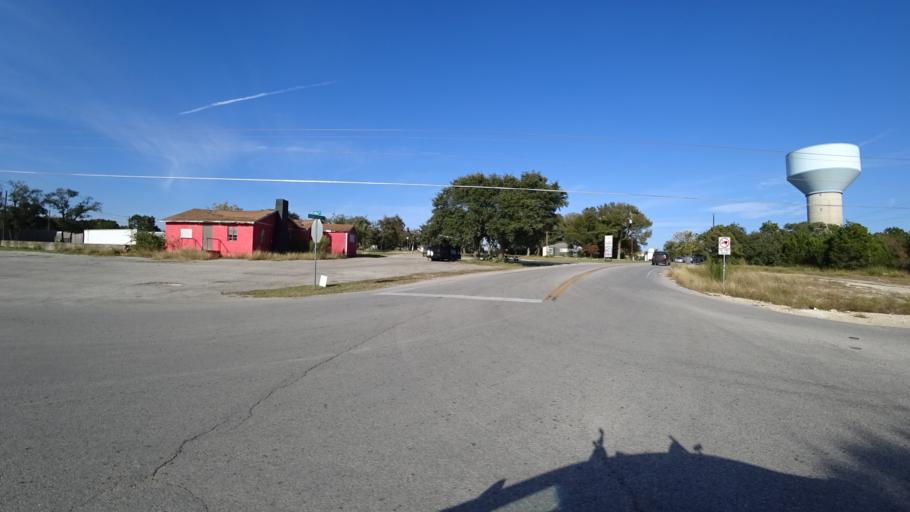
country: US
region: Texas
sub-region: Travis County
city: Bee Cave
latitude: 30.2462
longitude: -97.9272
